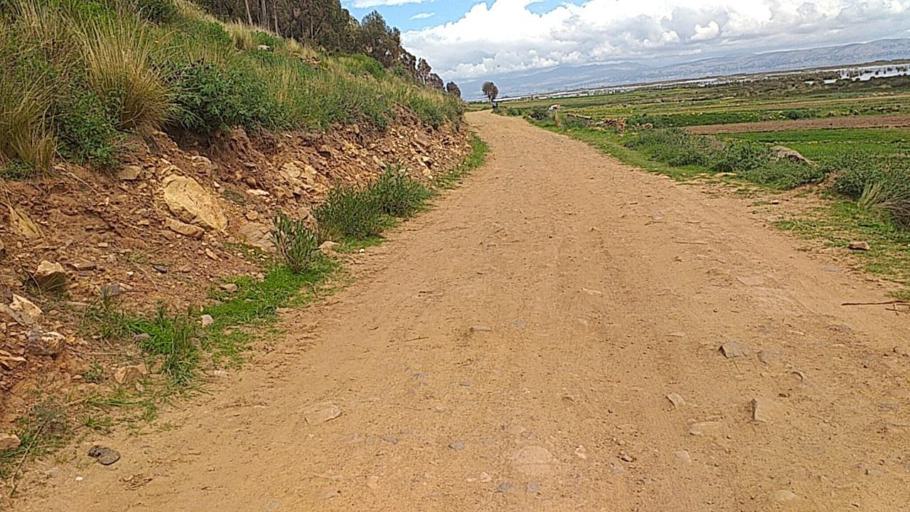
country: BO
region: La Paz
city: Batallas
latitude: -16.3325
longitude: -68.6385
